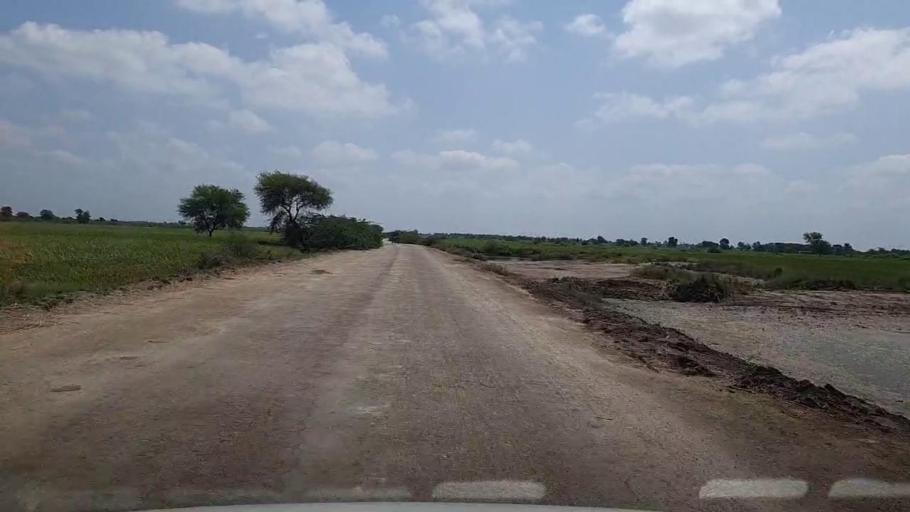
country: PK
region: Sindh
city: Talhar
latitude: 24.8868
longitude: 68.7038
